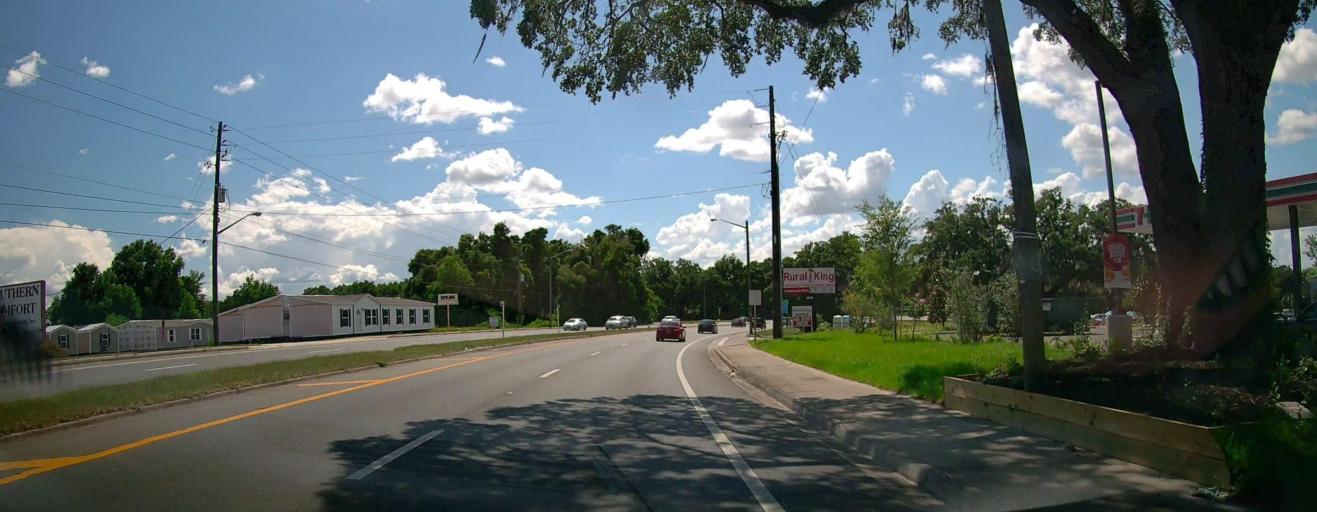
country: US
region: Florida
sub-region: Marion County
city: Ocala
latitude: 29.1967
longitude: -82.1694
